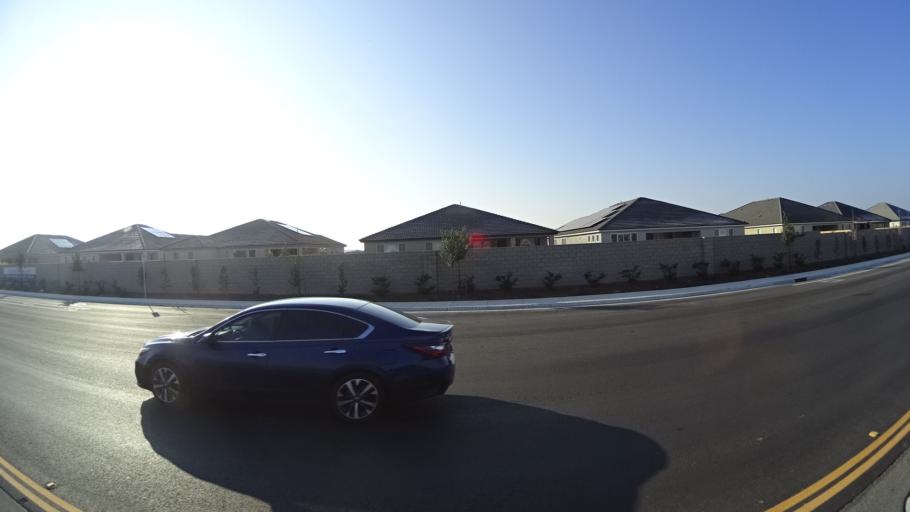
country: US
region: California
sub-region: Kern County
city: Greenacres
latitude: 35.2962
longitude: -119.1133
